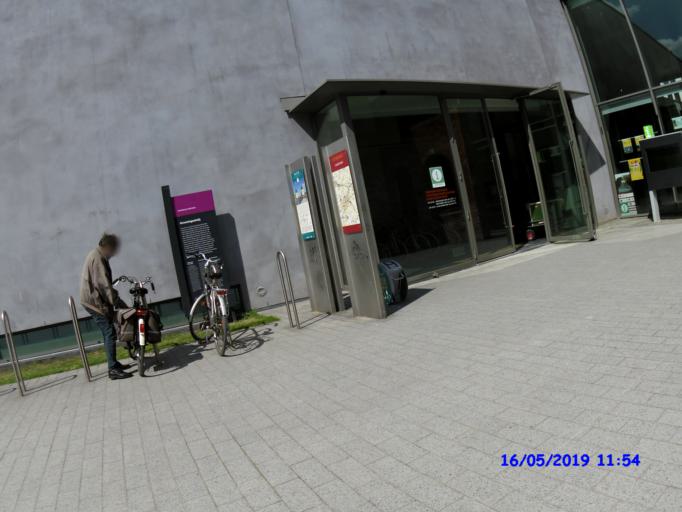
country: BE
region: Flanders
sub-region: Provincie West-Vlaanderen
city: Kortrijk
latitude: 50.8295
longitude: 3.2698
